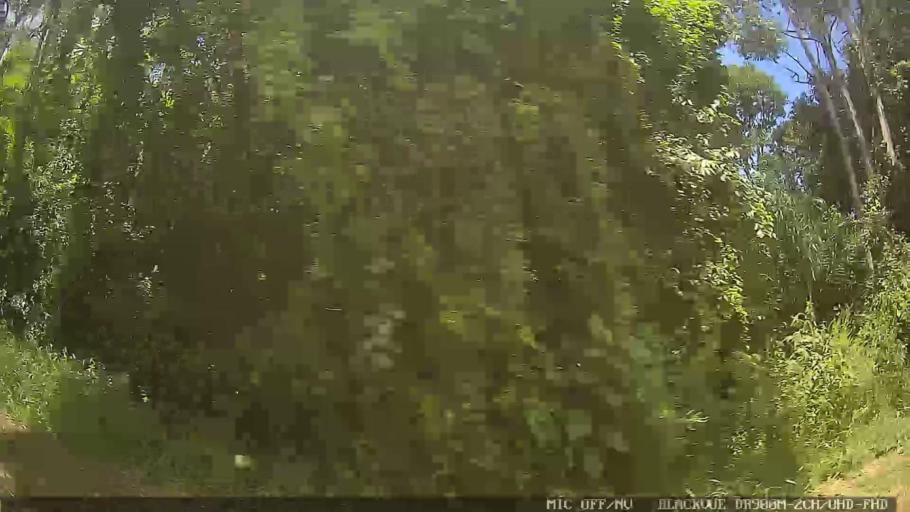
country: BR
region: Minas Gerais
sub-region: Extrema
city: Extrema
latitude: -22.7581
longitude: -46.4346
